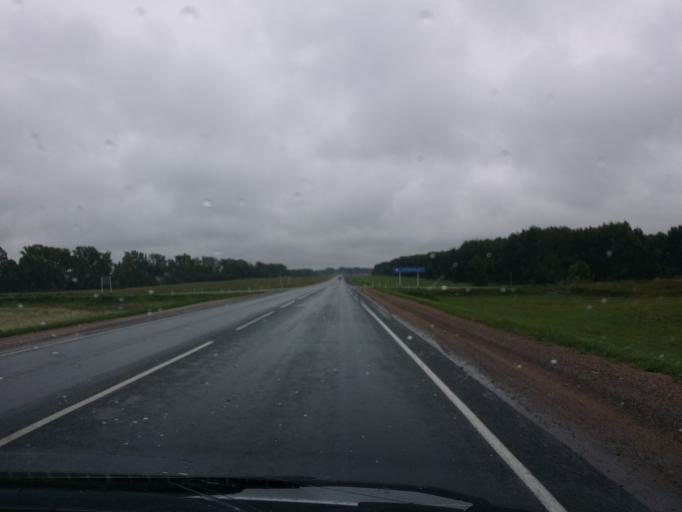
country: RU
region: Altai Krai
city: Bayunovskiye Klyuchi
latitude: 53.2931
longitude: 84.3046
